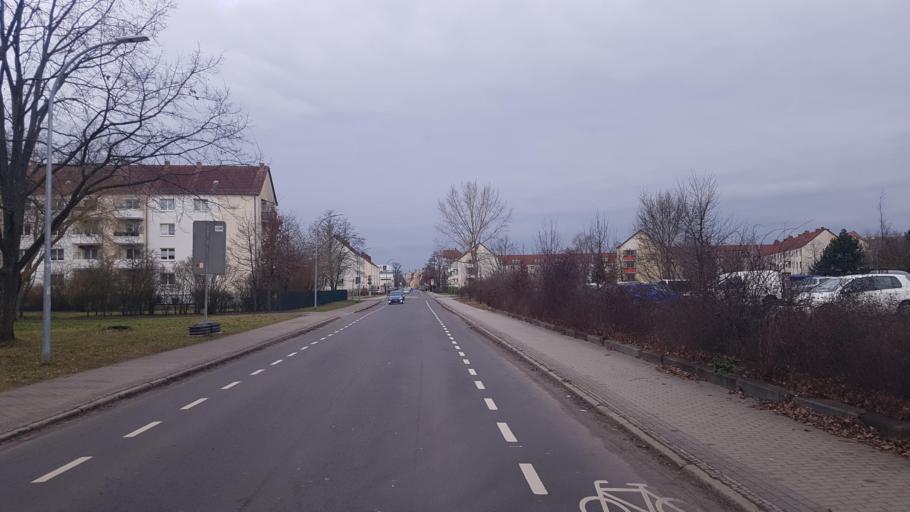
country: DE
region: Brandenburg
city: Oranienburg
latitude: 52.7505
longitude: 13.2489
